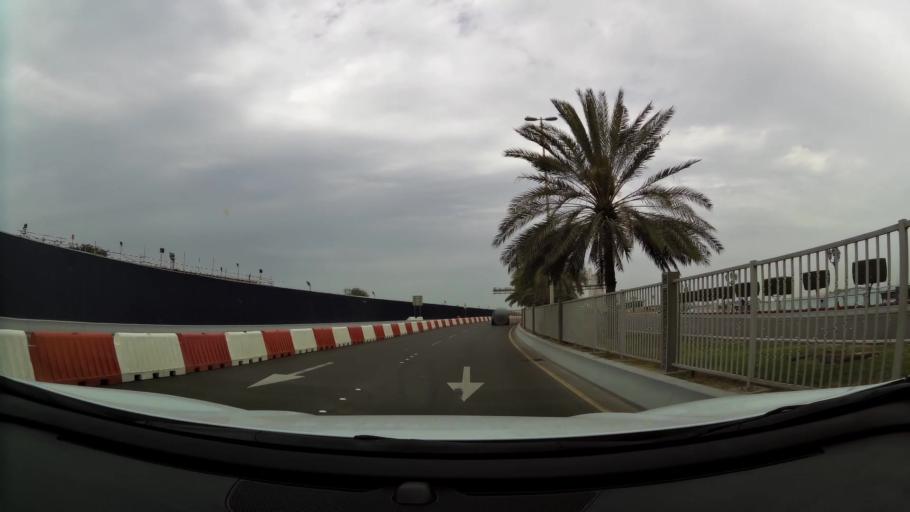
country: AE
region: Abu Dhabi
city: Abu Dhabi
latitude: 24.4645
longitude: 54.3231
